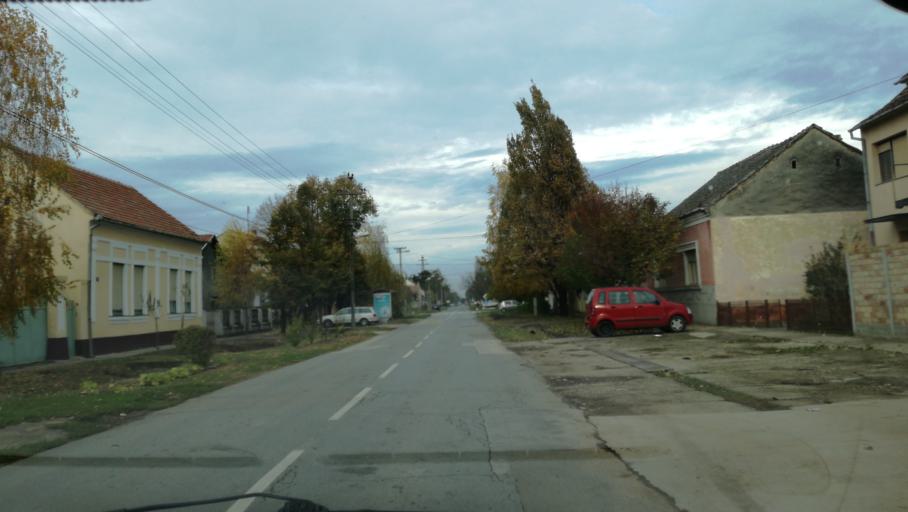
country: RS
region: Autonomna Pokrajina Vojvodina
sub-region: Severnobanatski Okrug
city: Kikinda
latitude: 45.8378
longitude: 20.4732
